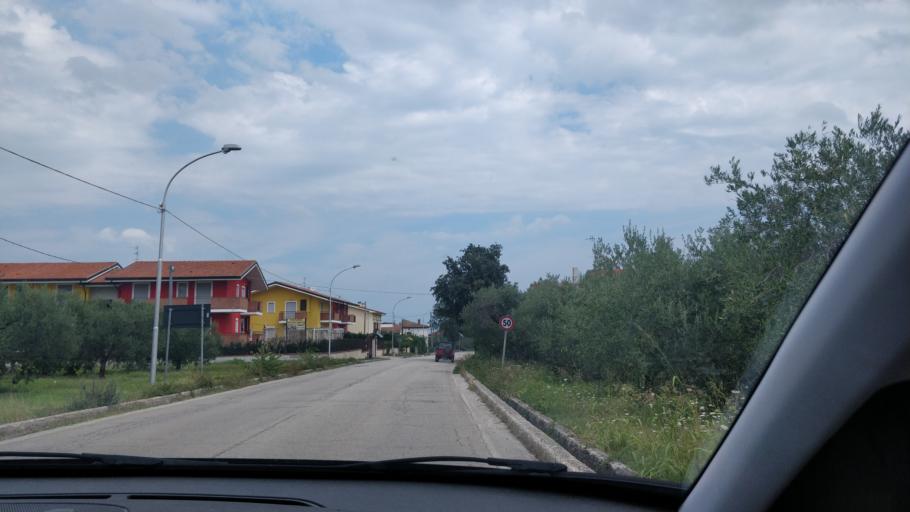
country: IT
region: Abruzzo
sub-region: Provincia di Chieti
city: San Vito Chietino
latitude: 42.2809
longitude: 14.4382
